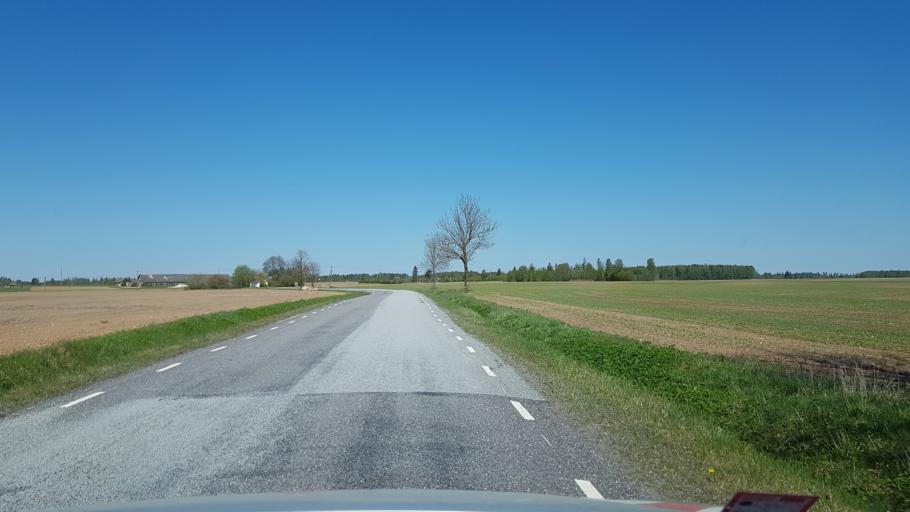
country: EE
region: Vorumaa
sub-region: Voru linn
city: Voru
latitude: 57.9163
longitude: 26.9553
